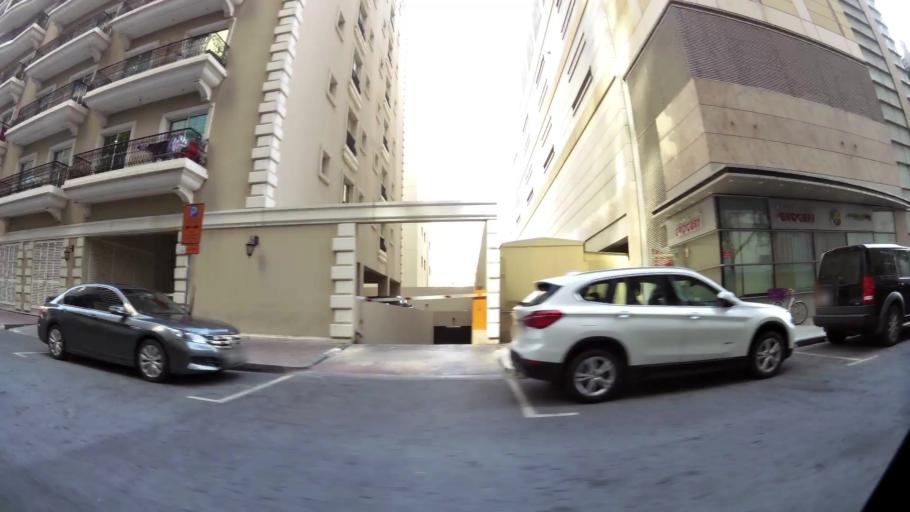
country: AE
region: Ash Shariqah
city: Sharjah
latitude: 25.2526
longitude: 55.3015
